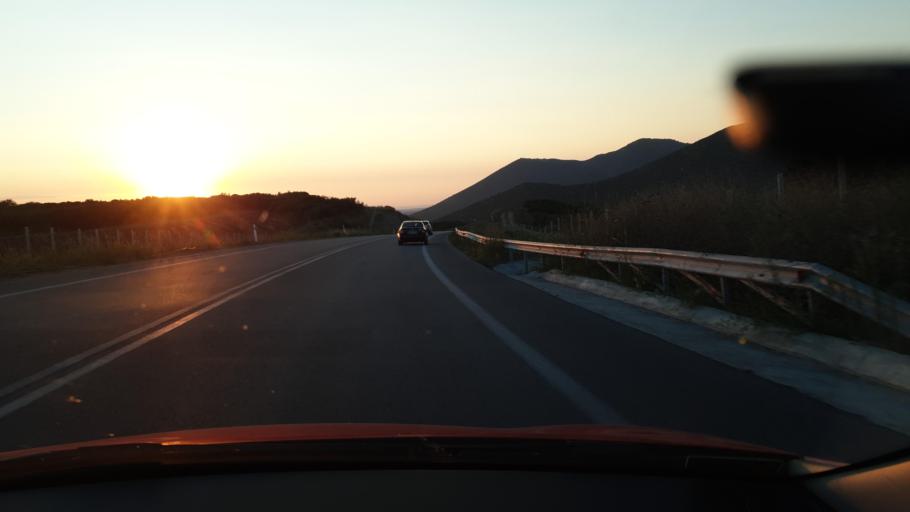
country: GR
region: Central Macedonia
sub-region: Nomos Chalkidikis
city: Galatista
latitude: 40.4624
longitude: 23.2230
